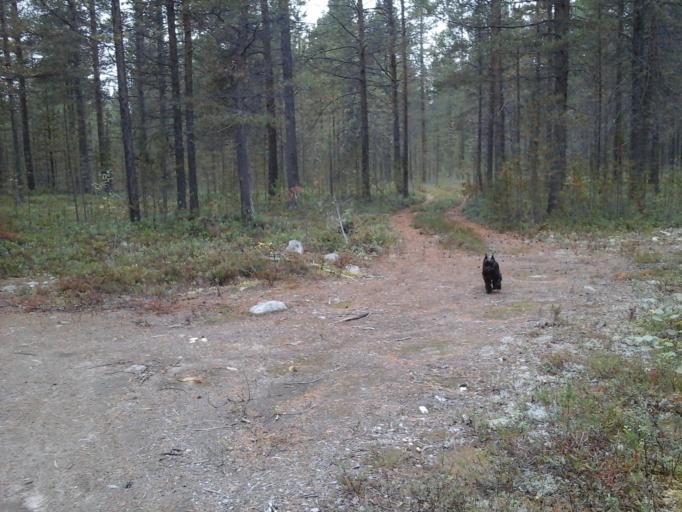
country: RU
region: Murmansk
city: Apatity
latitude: 67.5232
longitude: 33.2514
